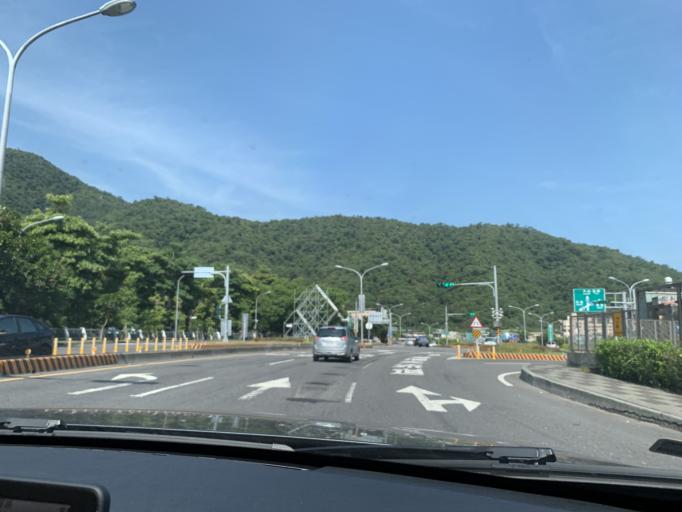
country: TW
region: Taiwan
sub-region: Yilan
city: Yilan
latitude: 24.5961
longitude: 121.8370
